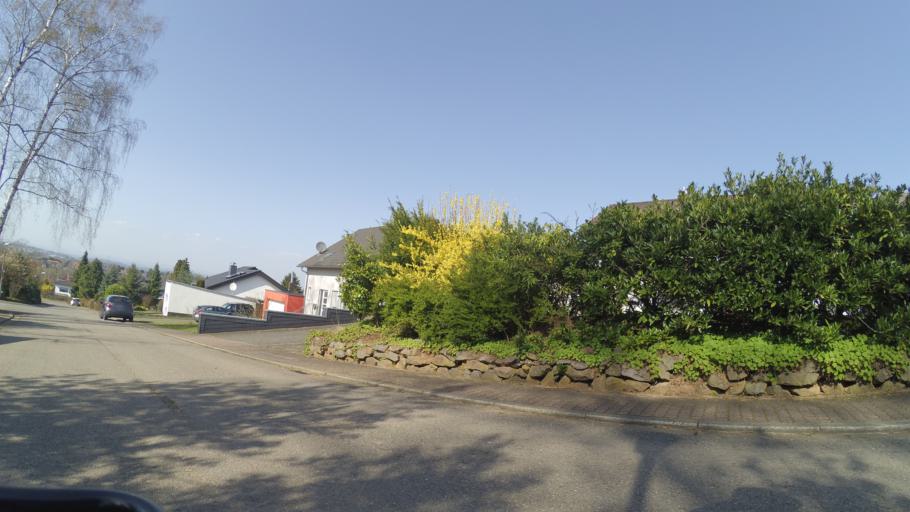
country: DE
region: Saarland
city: Merchweiler
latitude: 49.3400
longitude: 7.0090
